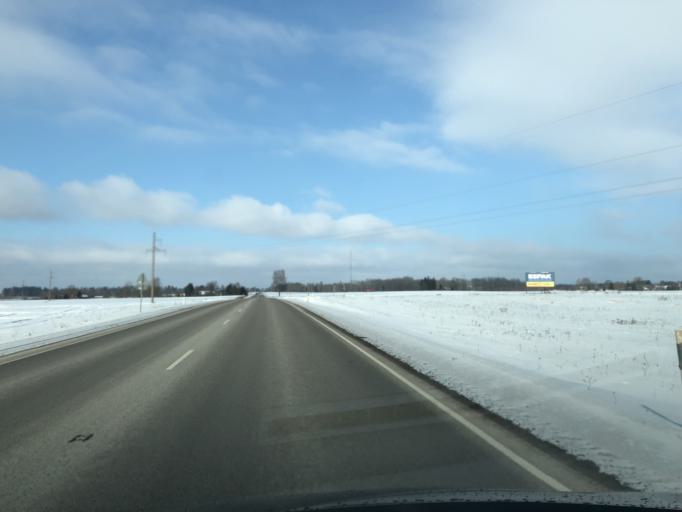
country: EE
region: Jaervamaa
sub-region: Paide linn
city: Paide
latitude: 58.8204
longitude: 25.7530
